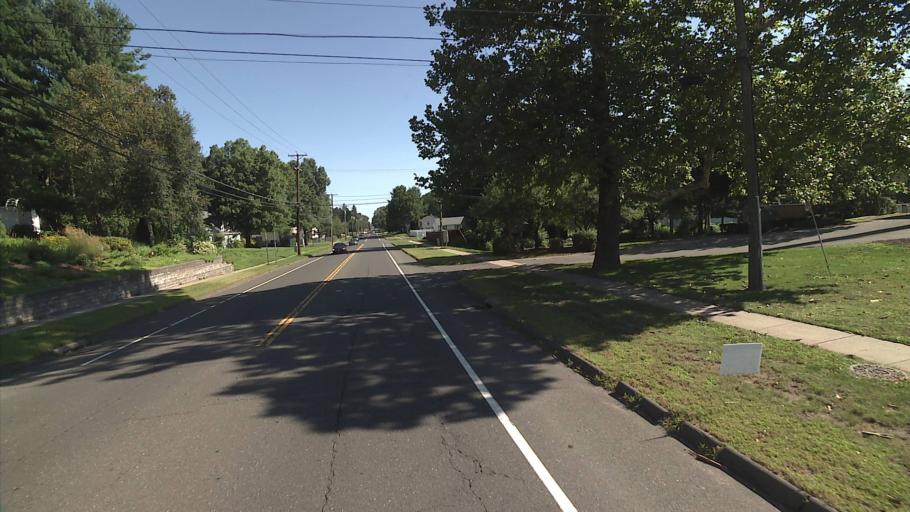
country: US
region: Connecticut
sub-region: New Haven County
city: Cheshire Village
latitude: 41.5112
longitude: -72.8992
